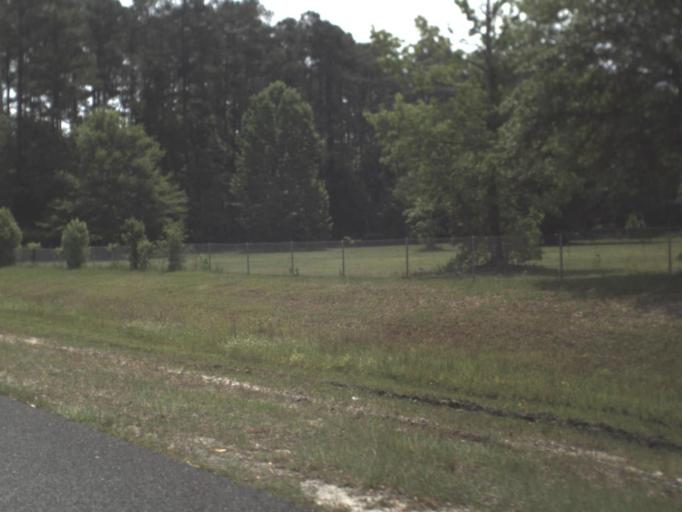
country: US
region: Florida
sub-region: Nassau County
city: Yulee
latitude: 30.6160
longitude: -81.7124
